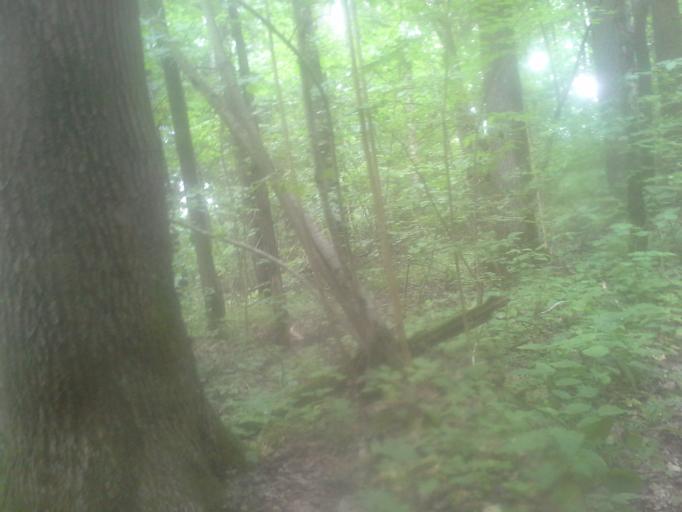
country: RU
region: Moskovskaya
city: Kievskij
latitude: 55.4474
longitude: 36.8569
